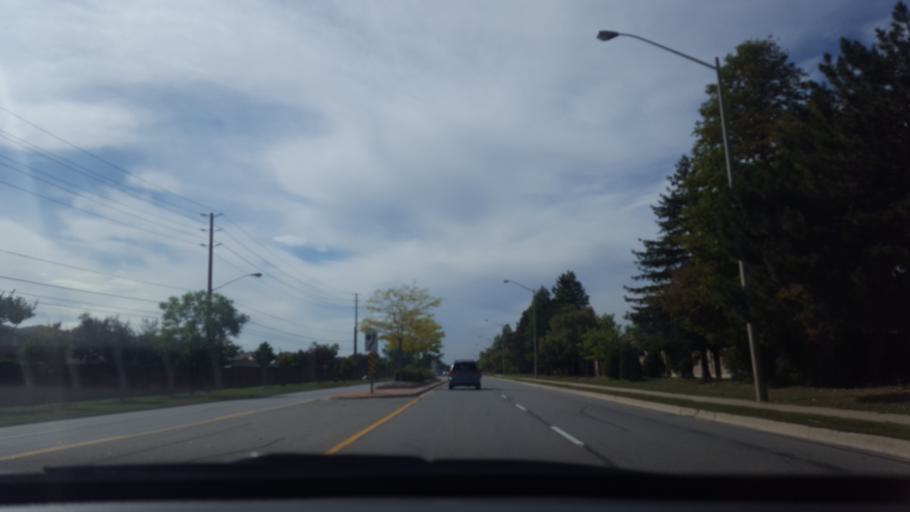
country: CA
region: Ontario
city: Vaughan
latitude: 43.8063
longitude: -79.5601
